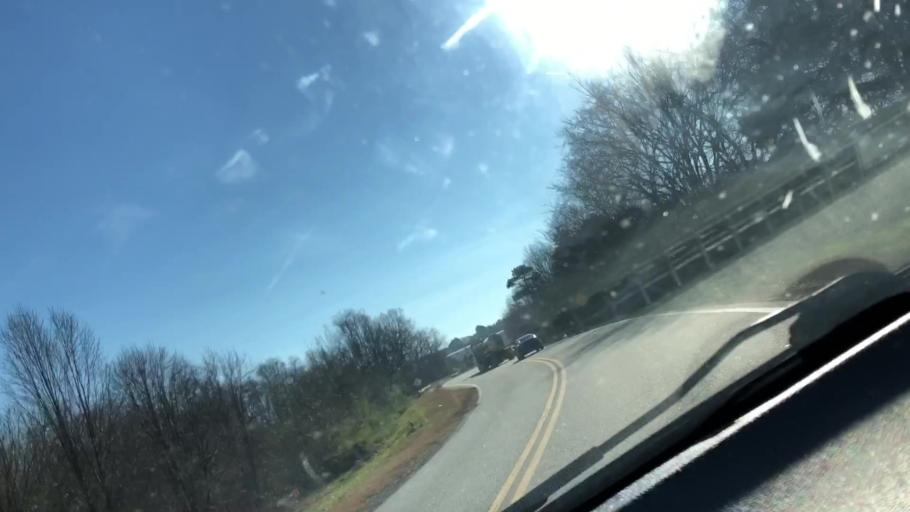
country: US
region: Georgia
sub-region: Bartow County
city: Cartersville
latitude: 34.2221
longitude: -84.8041
